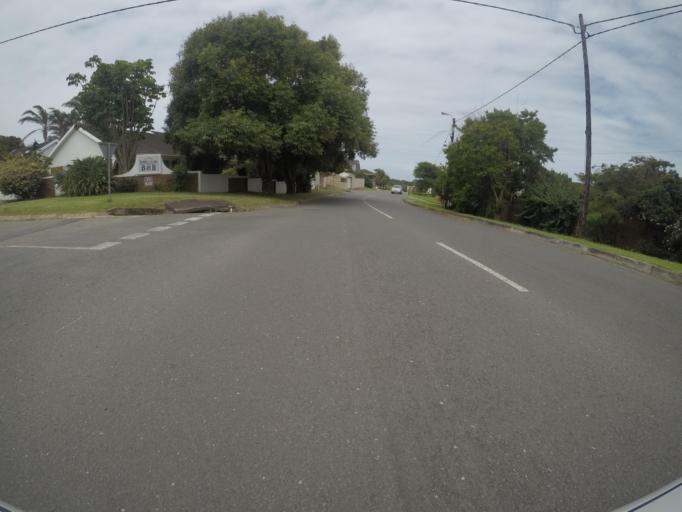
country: ZA
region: Eastern Cape
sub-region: Buffalo City Metropolitan Municipality
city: East London
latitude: -32.9805
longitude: 27.9493
